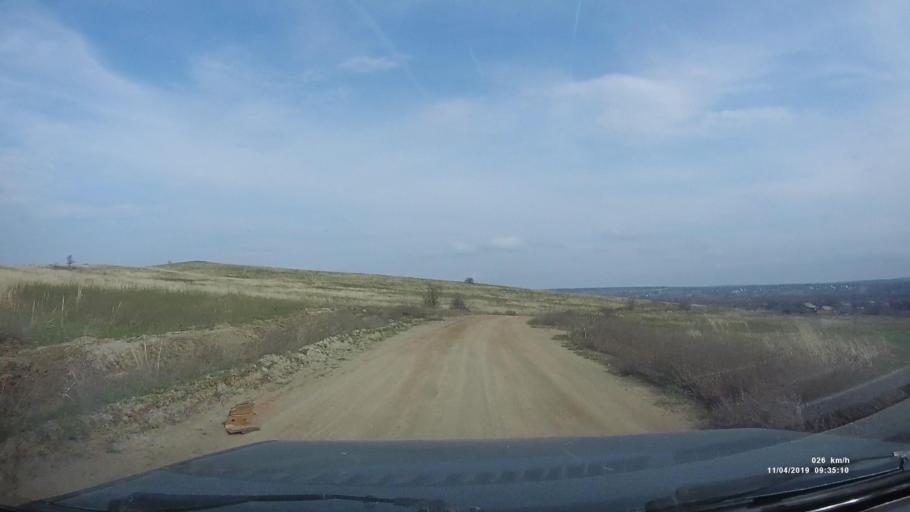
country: RU
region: Rostov
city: Staraya Stanitsa
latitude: 48.2713
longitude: 40.3715
